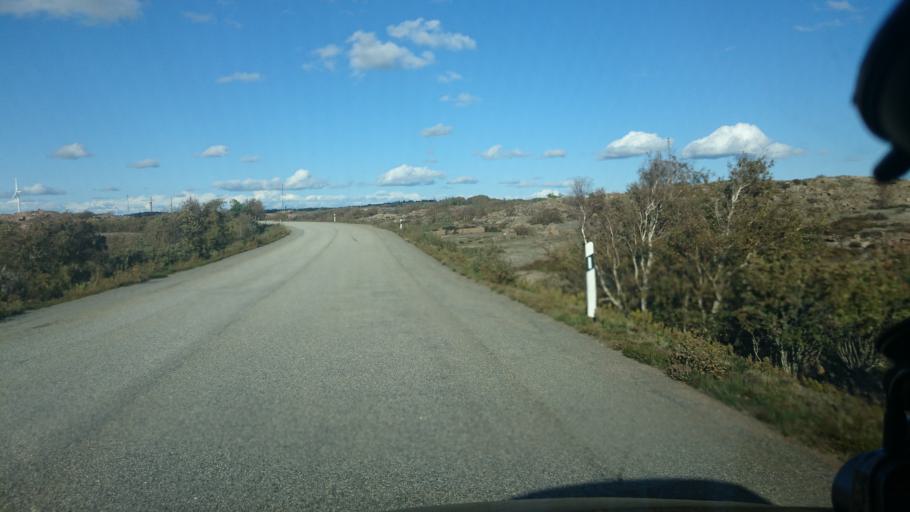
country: SE
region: Vaestra Goetaland
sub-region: Lysekils Kommun
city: Lysekil
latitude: 58.3173
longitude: 11.4084
